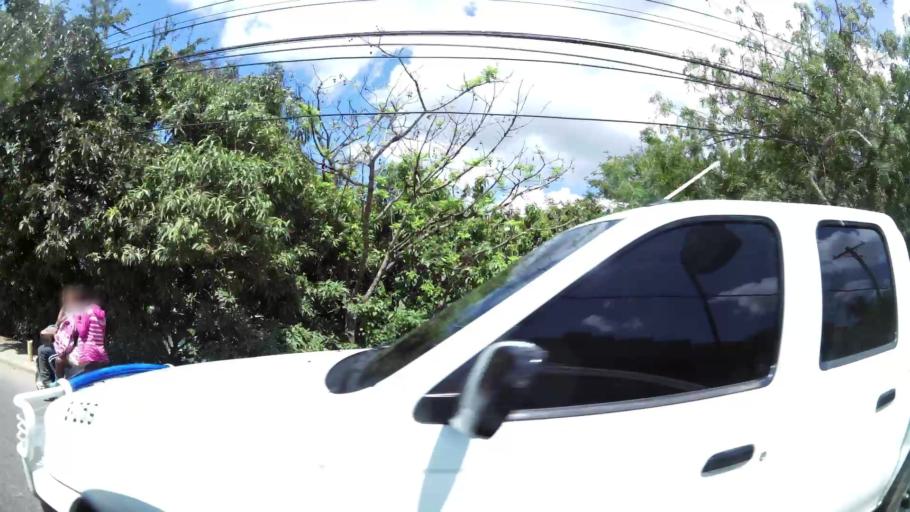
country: DO
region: Santiago
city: Santiago de los Caballeros
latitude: 19.4101
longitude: -70.6724
